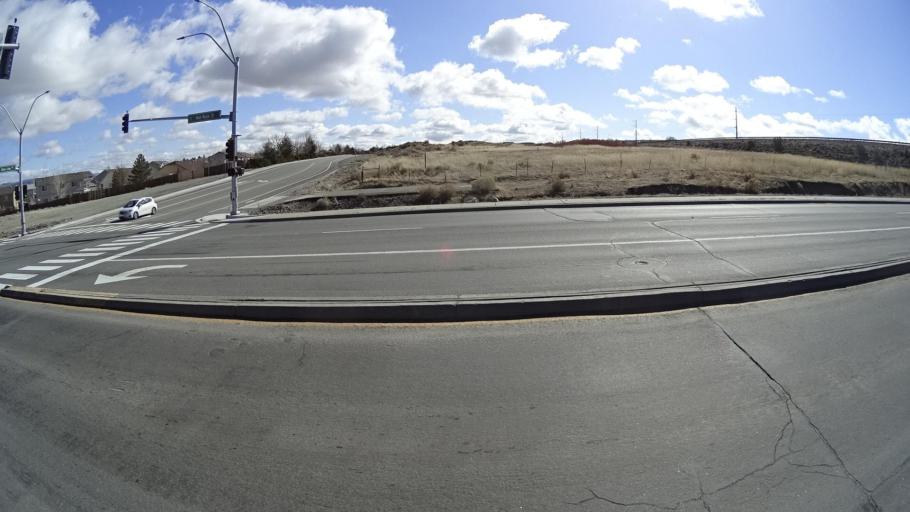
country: US
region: Nevada
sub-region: Washoe County
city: Lemmon Valley
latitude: 39.6276
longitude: -119.9168
